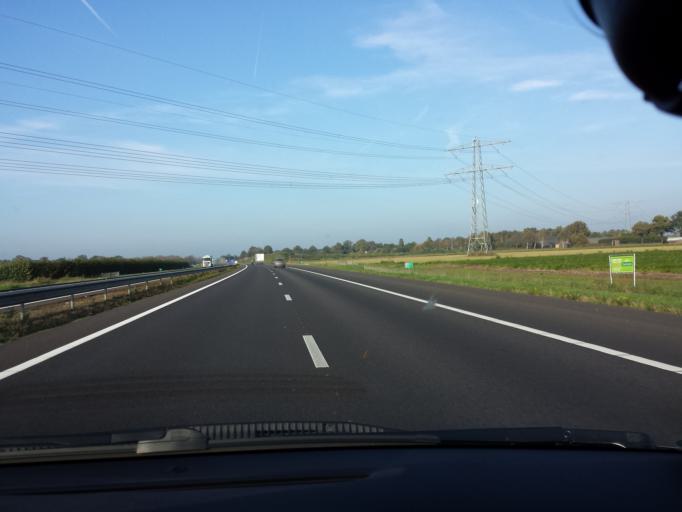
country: NL
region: Limburg
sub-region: Gemeente Peel en Maas
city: Maasbree
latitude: 51.4347
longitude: 6.0976
